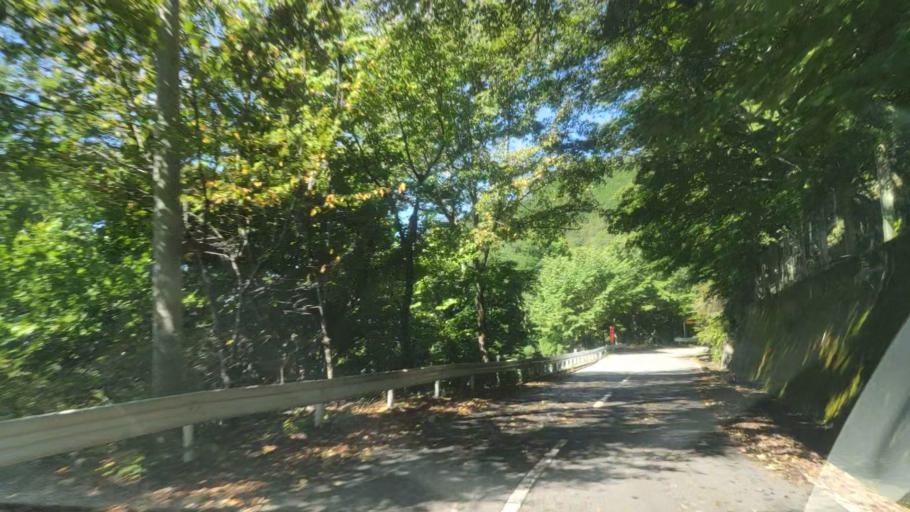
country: JP
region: Yamanashi
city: Fujikawaguchiko
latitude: 35.5662
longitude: 138.7851
